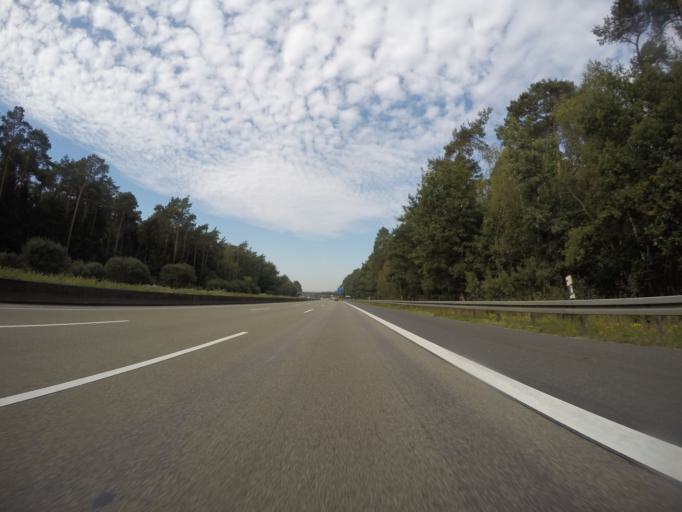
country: DE
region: Hesse
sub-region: Regierungsbezirk Darmstadt
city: Rodgau
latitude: 50.0545
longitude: 8.9123
